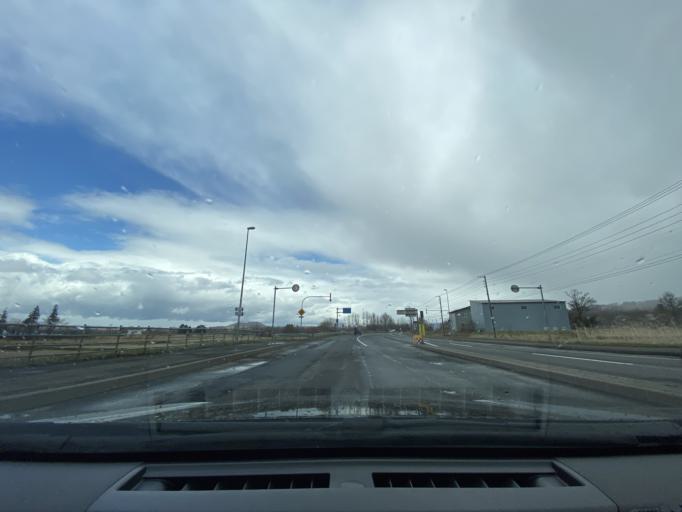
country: JP
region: Hokkaido
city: Fukagawa
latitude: 43.7000
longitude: 142.0724
